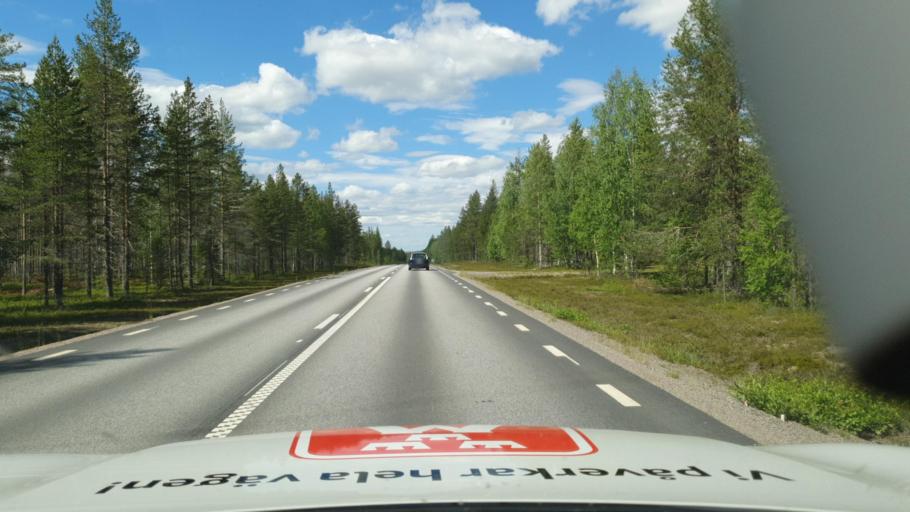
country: SE
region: Vaesterbotten
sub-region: Skelleftea Kommun
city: Langsele
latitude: 65.0115
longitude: 20.1636
